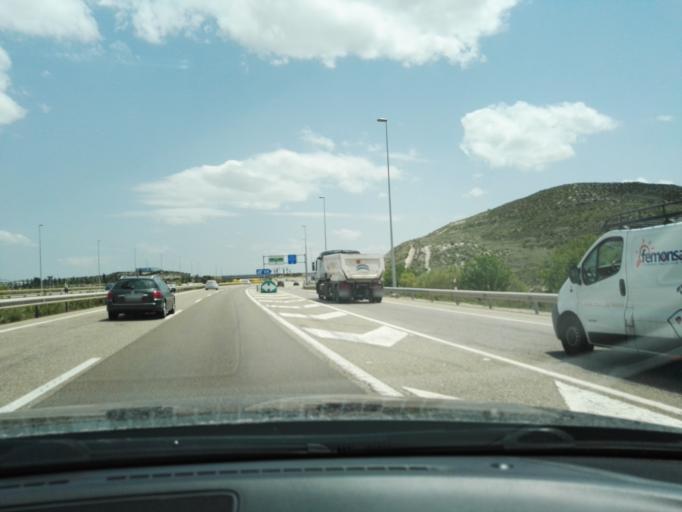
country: ES
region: Aragon
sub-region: Provincia de Zaragoza
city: Montecanal
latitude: 41.6172
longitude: -0.9382
